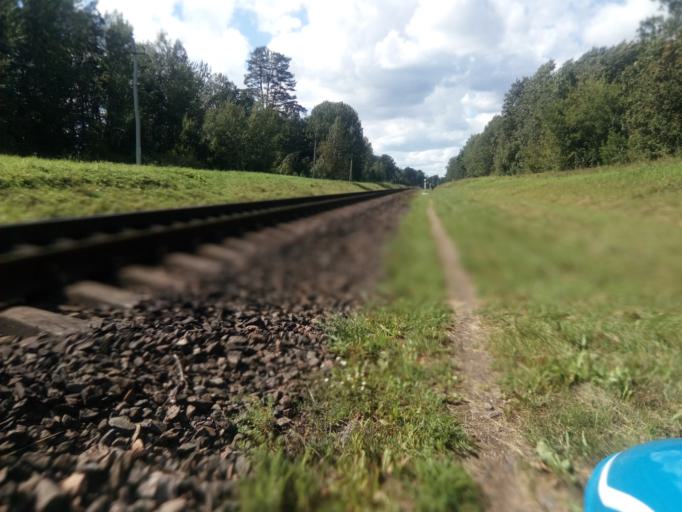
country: BY
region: Vitebsk
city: Dzisna
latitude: 55.6777
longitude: 28.3015
